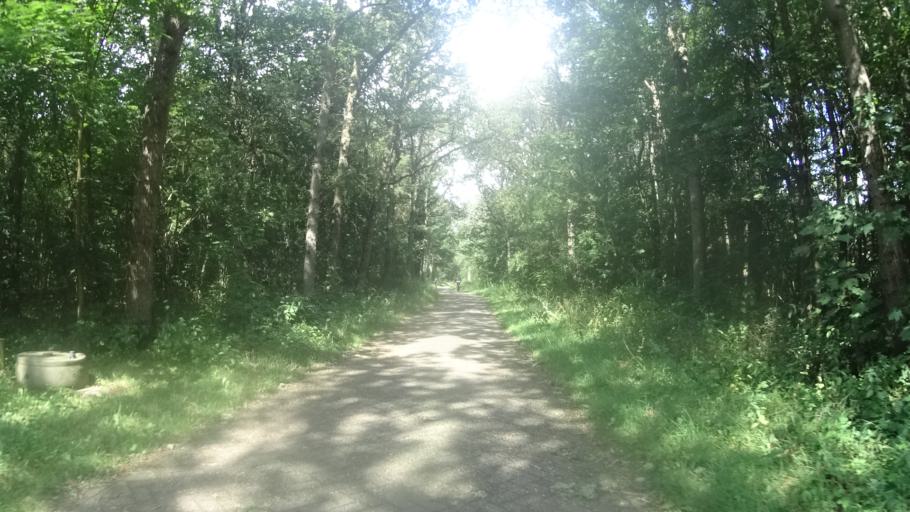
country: NL
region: North Holland
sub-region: Gemeente Castricum
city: Castricum
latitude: 52.5630
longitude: 4.6404
